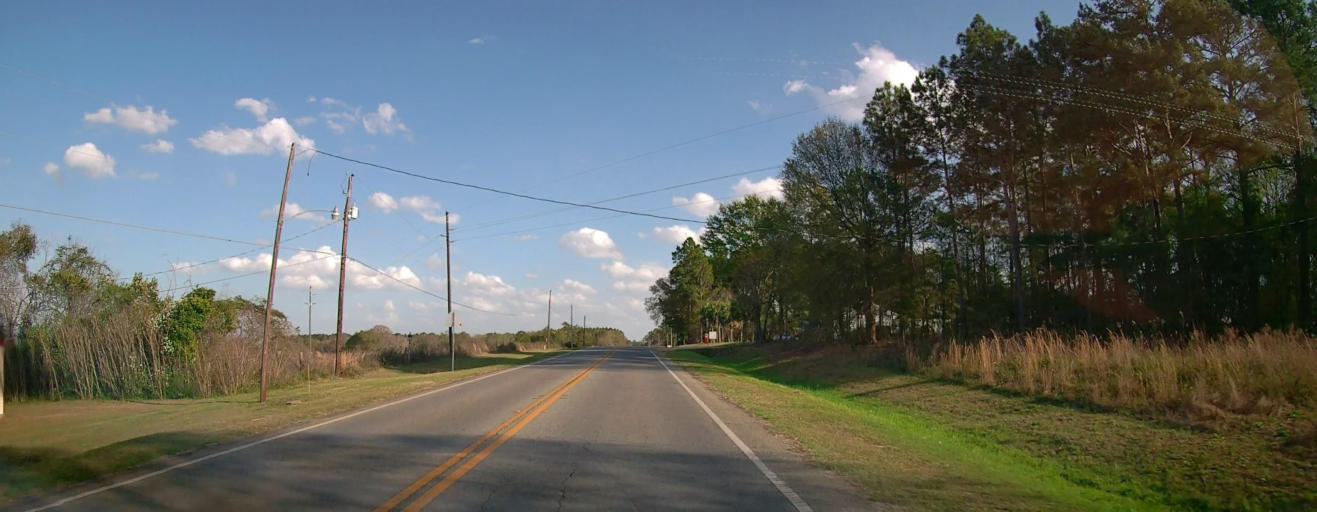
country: US
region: Georgia
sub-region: Toombs County
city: Lyons
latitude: 32.1945
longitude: -82.3095
